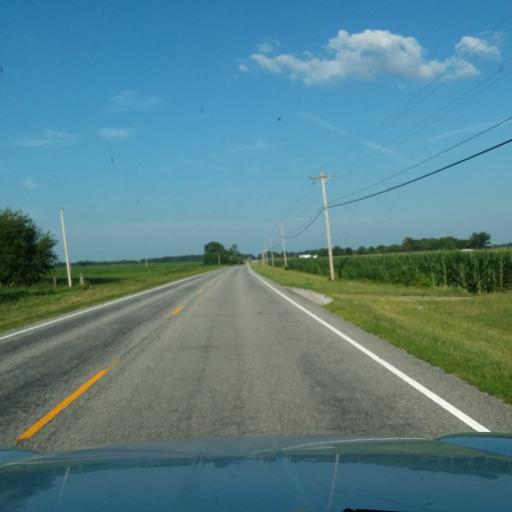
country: US
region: Indiana
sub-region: Johnson County
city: Franklin
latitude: 39.4118
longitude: -86.0381
